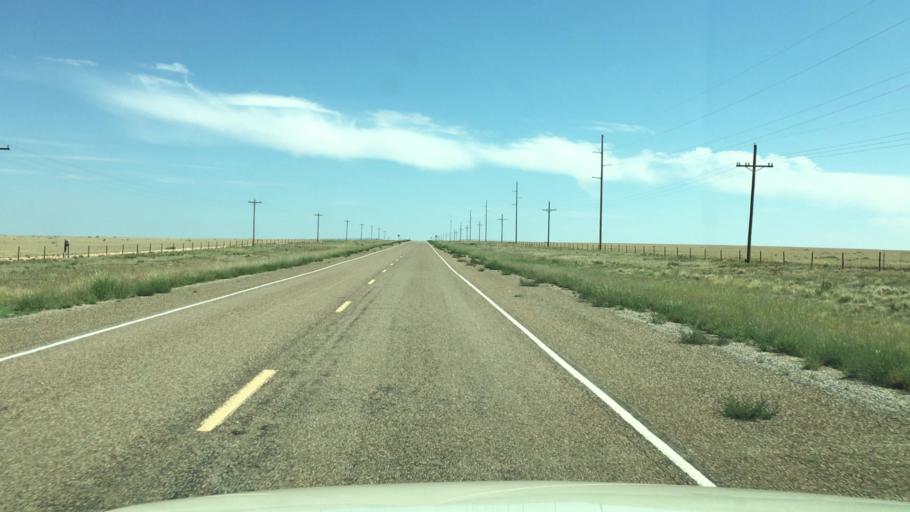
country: US
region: New Mexico
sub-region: Chaves County
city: Roswell
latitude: 33.9408
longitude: -104.5926
